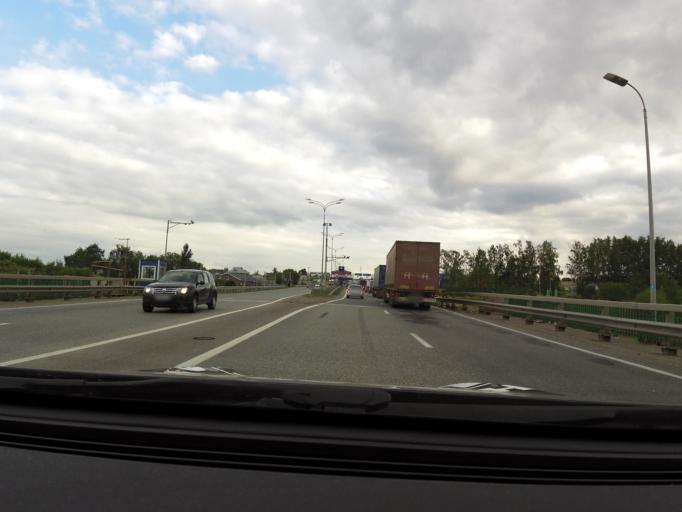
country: RU
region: Tatarstan
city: Osinovo
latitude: 55.7816
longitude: 48.8403
